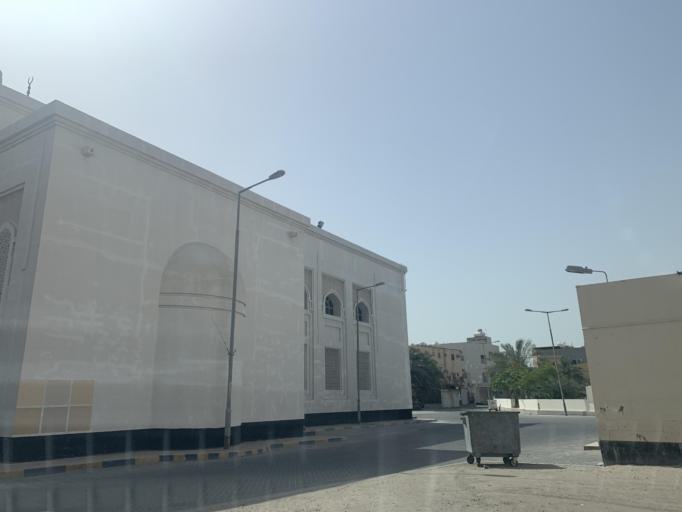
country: BH
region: Northern
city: Sitrah
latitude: 26.1610
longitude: 50.6075
